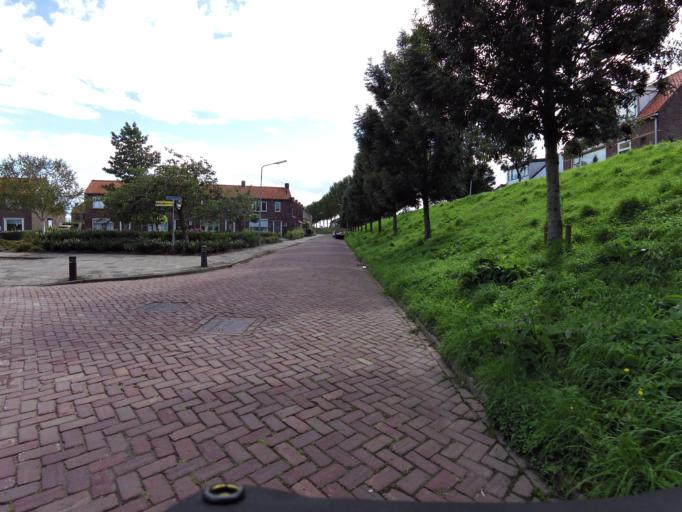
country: NL
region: North Brabant
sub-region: Gemeente Steenbergen
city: Dinteloord
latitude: 51.6860
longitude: 4.2805
